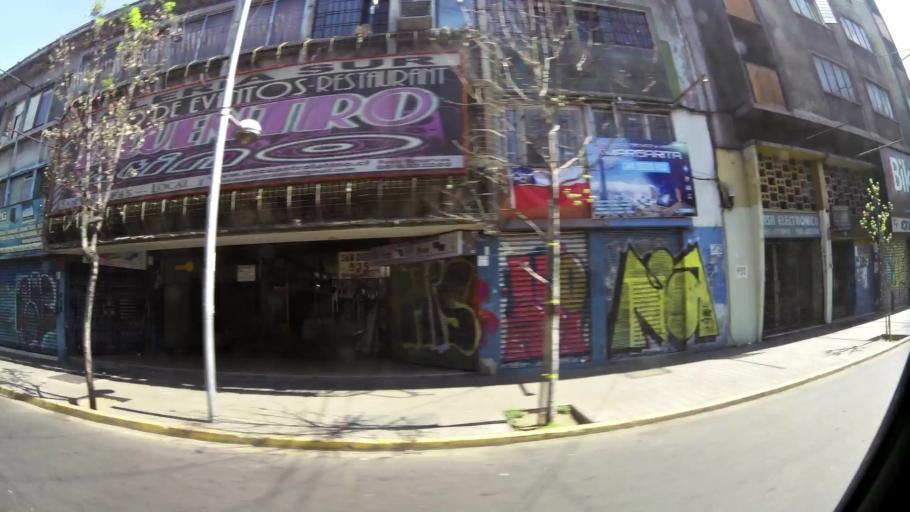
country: CL
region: Santiago Metropolitan
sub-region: Provincia de Santiago
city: Santiago
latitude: -33.4576
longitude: -70.6495
